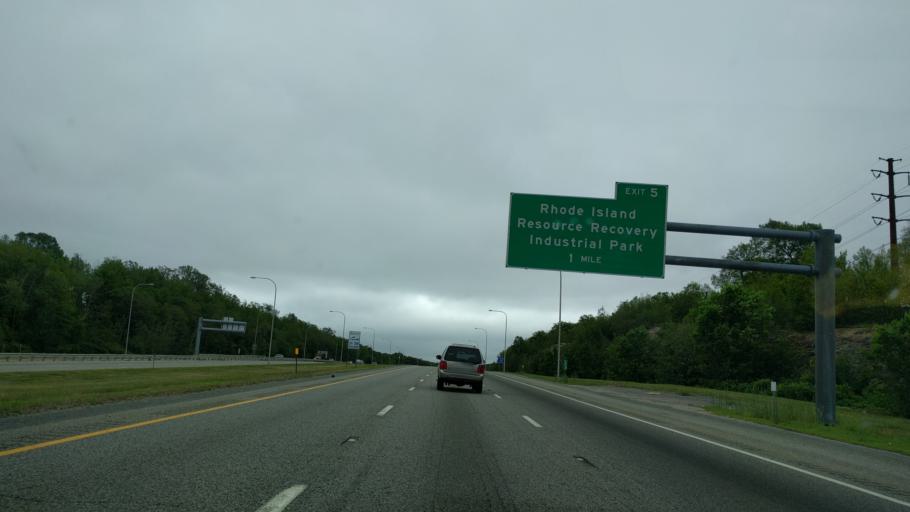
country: US
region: Rhode Island
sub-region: Providence County
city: Johnston
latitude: 41.8188
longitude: -71.5121
